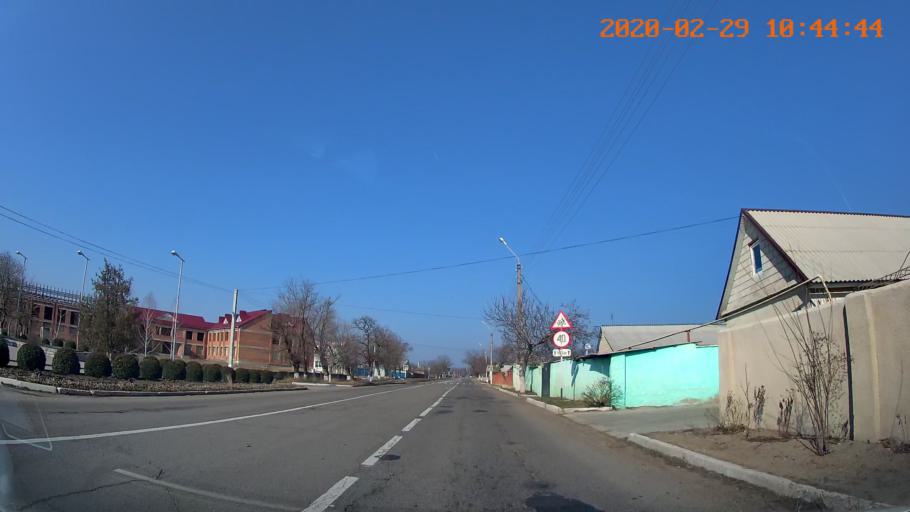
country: MD
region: Telenesti
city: Grigoriopol
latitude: 47.0718
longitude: 29.3911
